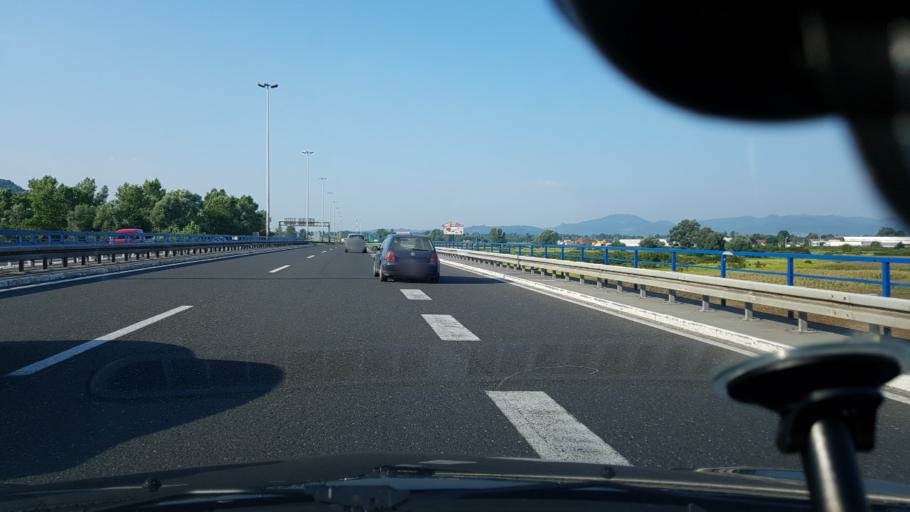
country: HR
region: Zagrebacka
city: Zapresic
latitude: 45.8505
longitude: 15.8248
